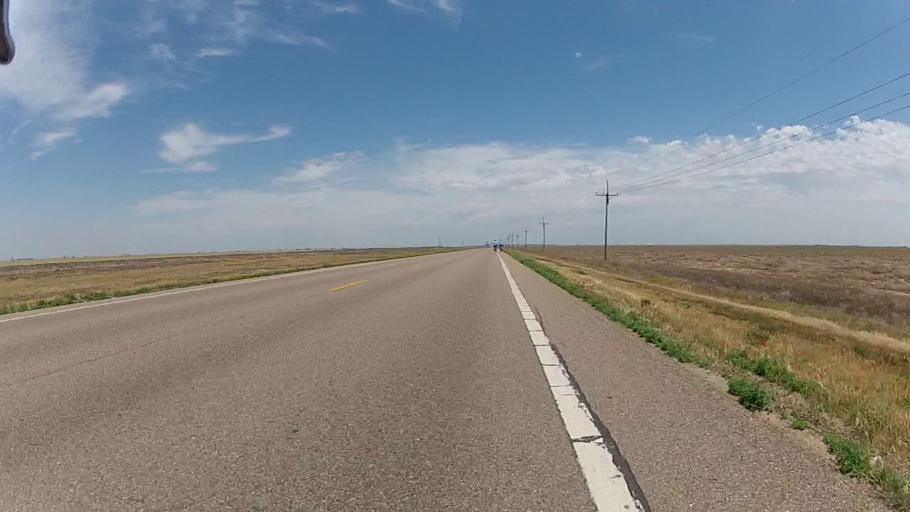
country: US
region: Kansas
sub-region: Haskell County
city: Satanta
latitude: 37.4616
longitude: -100.9221
